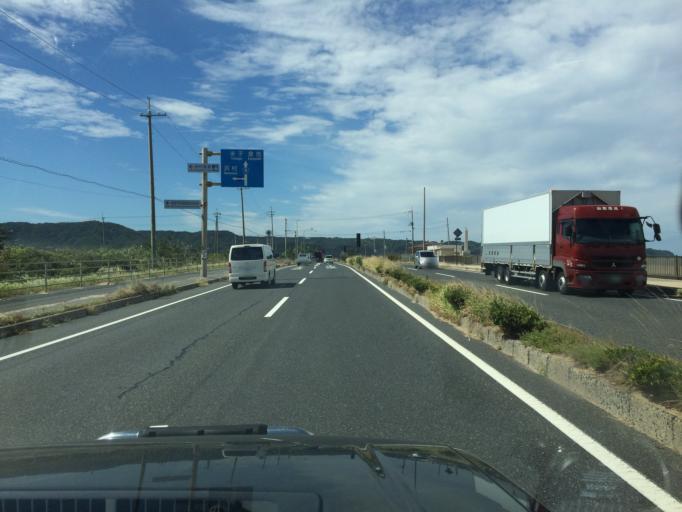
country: JP
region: Tottori
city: Tottori
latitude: 35.5180
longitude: 134.0521
